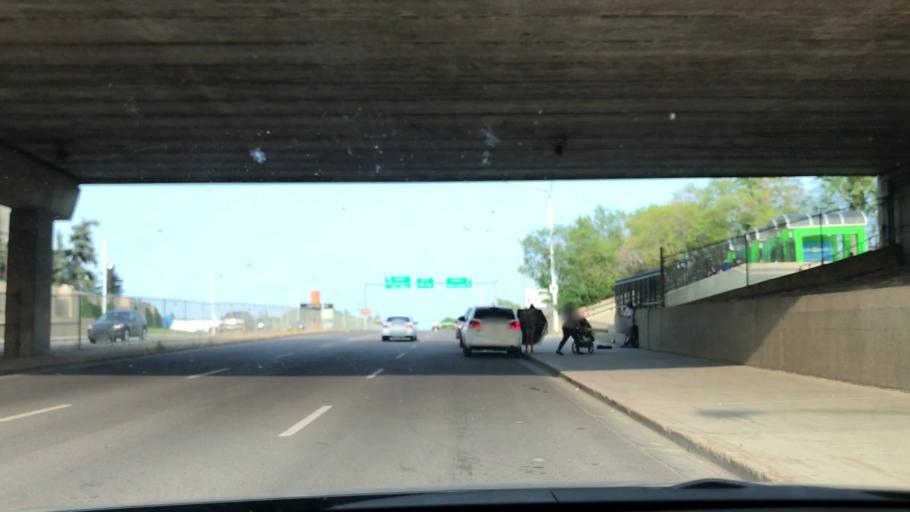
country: CA
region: Alberta
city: Edmonton
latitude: 53.5703
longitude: -113.4574
